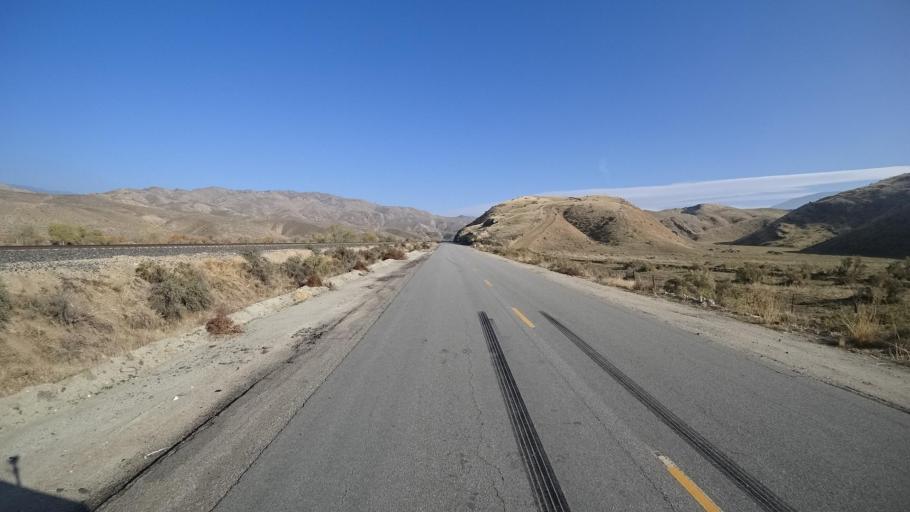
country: US
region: California
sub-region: Kern County
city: Arvin
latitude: 35.3242
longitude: -118.7199
